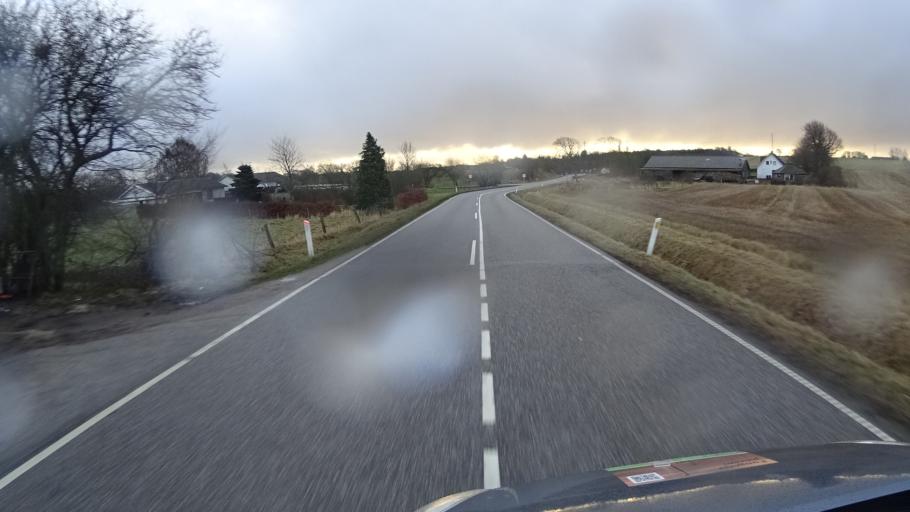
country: DK
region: South Denmark
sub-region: Vejle Kommune
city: Vejle
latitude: 55.7421
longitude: 9.5033
